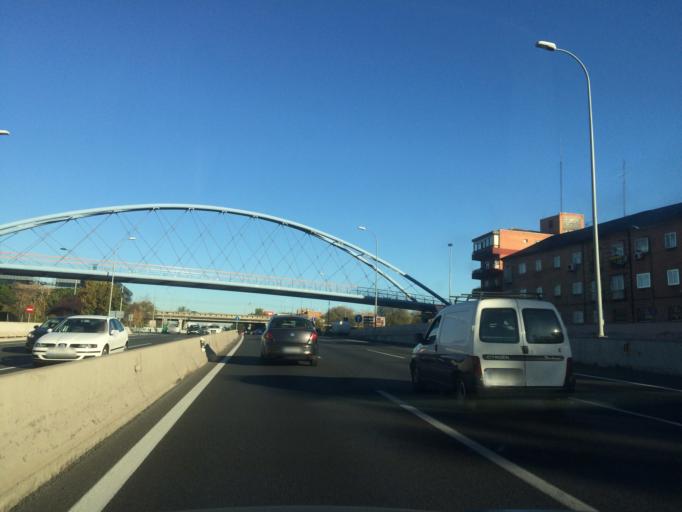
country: ES
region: Madrid
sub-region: Provincia de Madrid
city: San Blas
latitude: 40.4496
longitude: -3.6072
